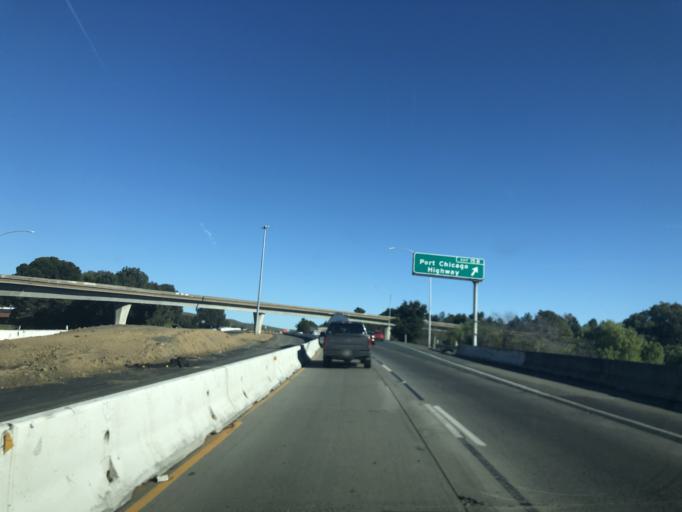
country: US
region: California
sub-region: Contra Costa County
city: Concord
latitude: 38.0043
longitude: -122.0398
